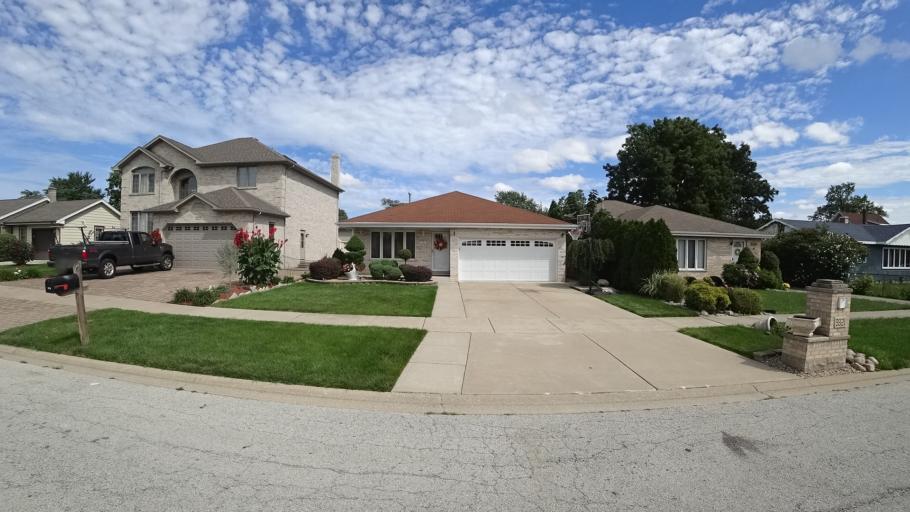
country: US
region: Illinois
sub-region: Cook County
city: Chicago Ridge
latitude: 41.7132
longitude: -87.7785
